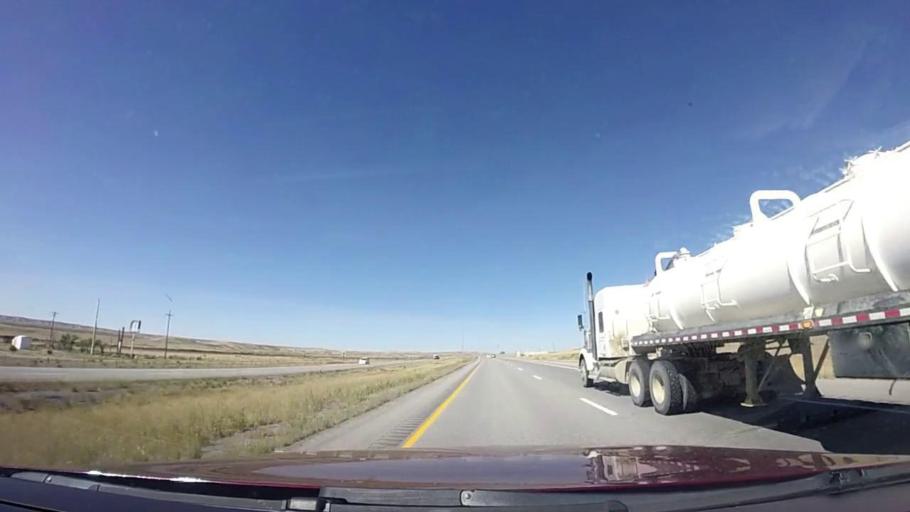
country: US
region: Wyoming
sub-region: Carbon County
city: Rawlins
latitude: 41.6539
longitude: -108.1185
